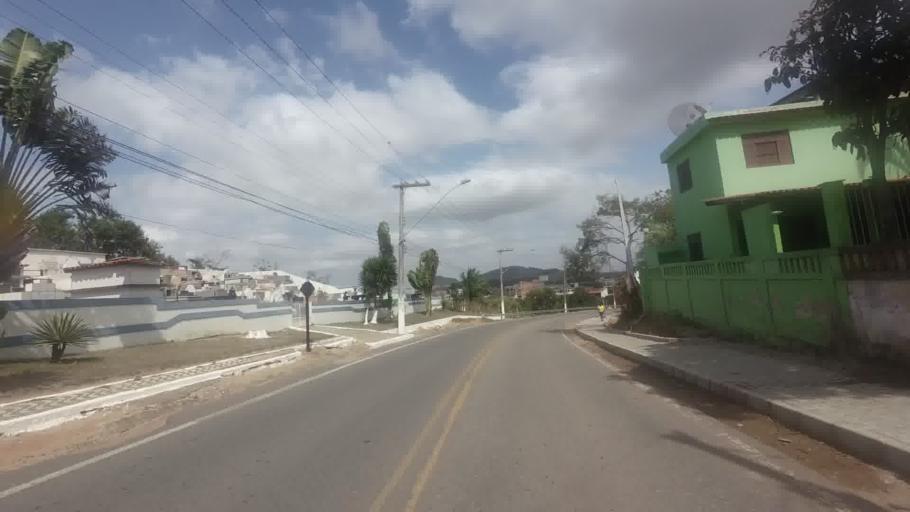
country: BR
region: Espirito Santo
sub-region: Piuma
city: Piuma
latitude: -20.8882
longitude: -40.7708
